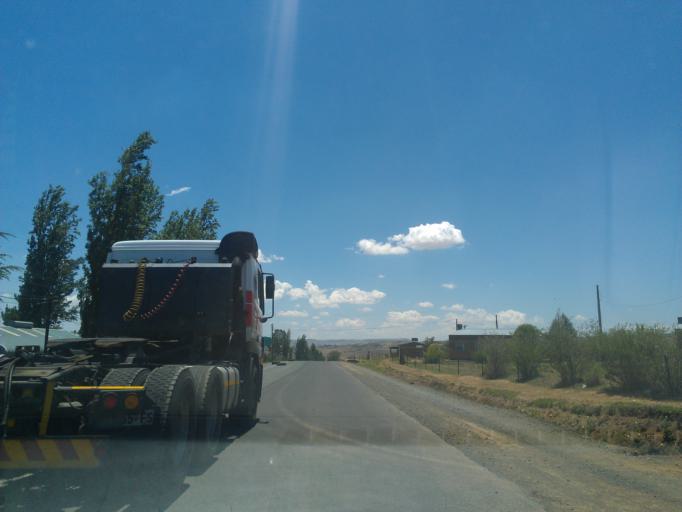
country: LS
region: Berea
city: Teyateyaneng
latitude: -29.1385
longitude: 27.7659
